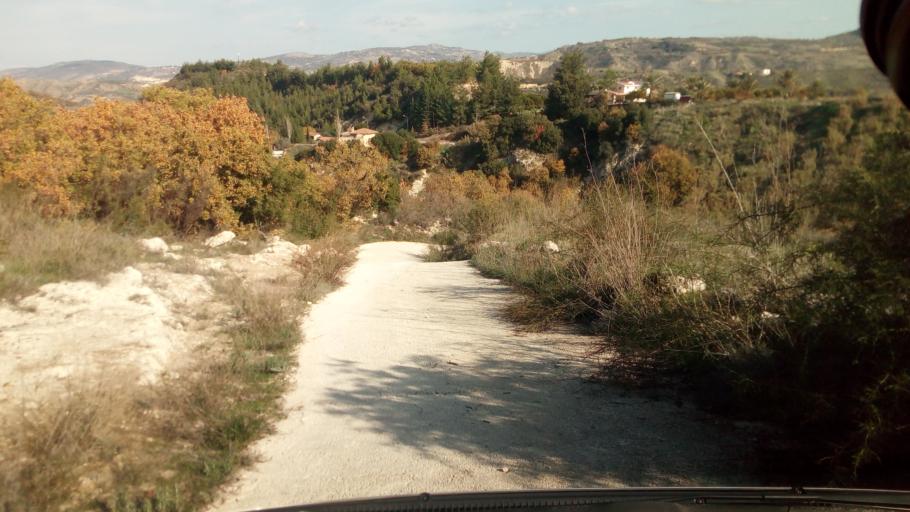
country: CY
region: Pafos
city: Pegeia
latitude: 34.9315
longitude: 32.4637
